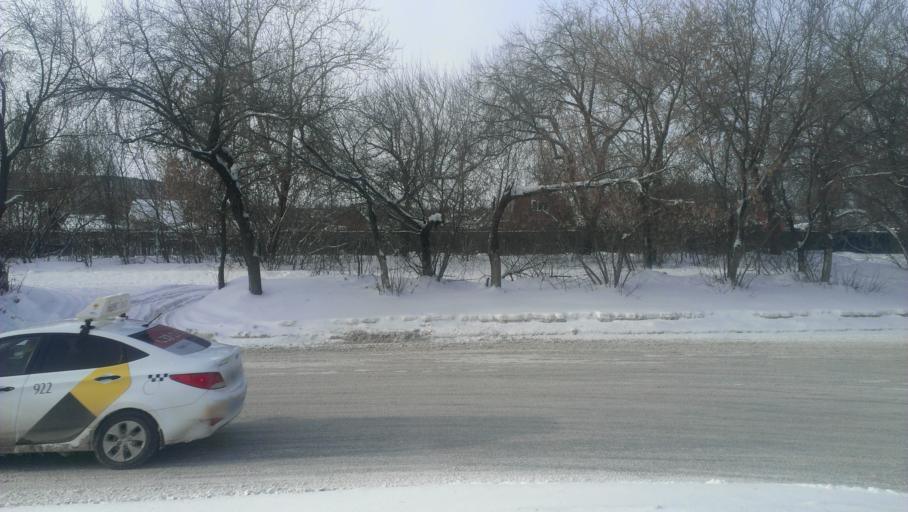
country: RU
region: Altai Krai
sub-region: Gorod Barnaulskiy
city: Barnaul
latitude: 53.3853
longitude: 83.6839
